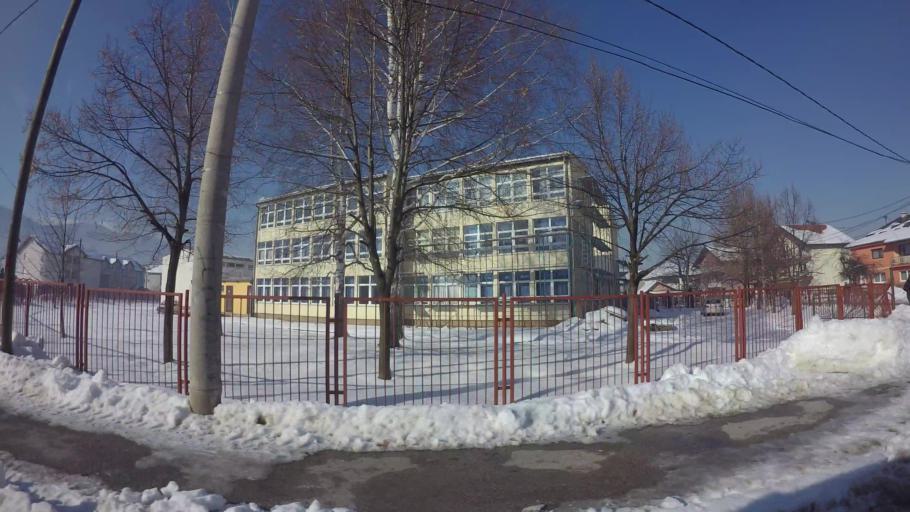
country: BA
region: Federation of Bosnia and Herzegovina
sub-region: Kanton Sarajevo
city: Sarajevo
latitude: 43.8101
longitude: 18.3146
